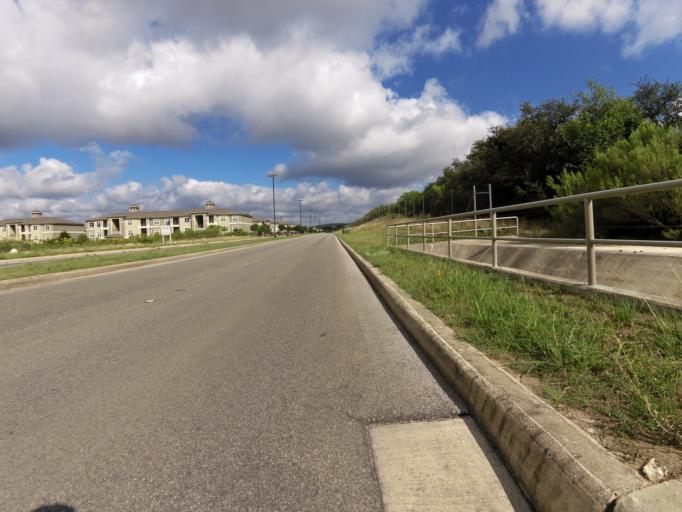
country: US
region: Texas
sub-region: Bexar County
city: Shavano Park
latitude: 29.5973
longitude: -98.5923
